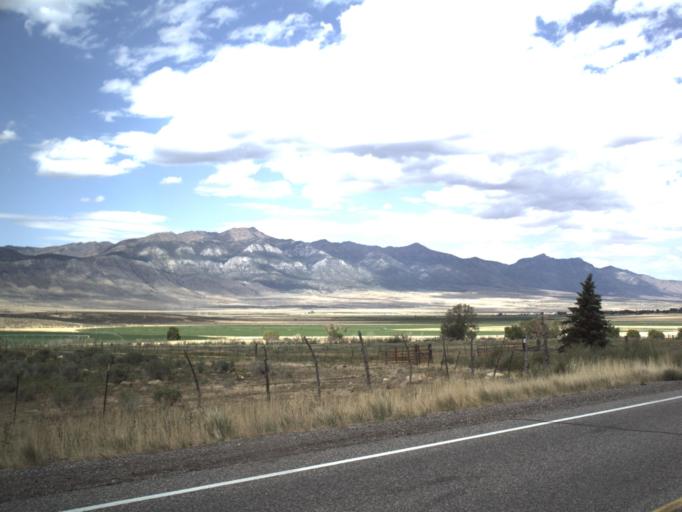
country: US
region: Utah
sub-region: Sanpete County
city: Gunnison
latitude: 39.2076
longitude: -112.0891
